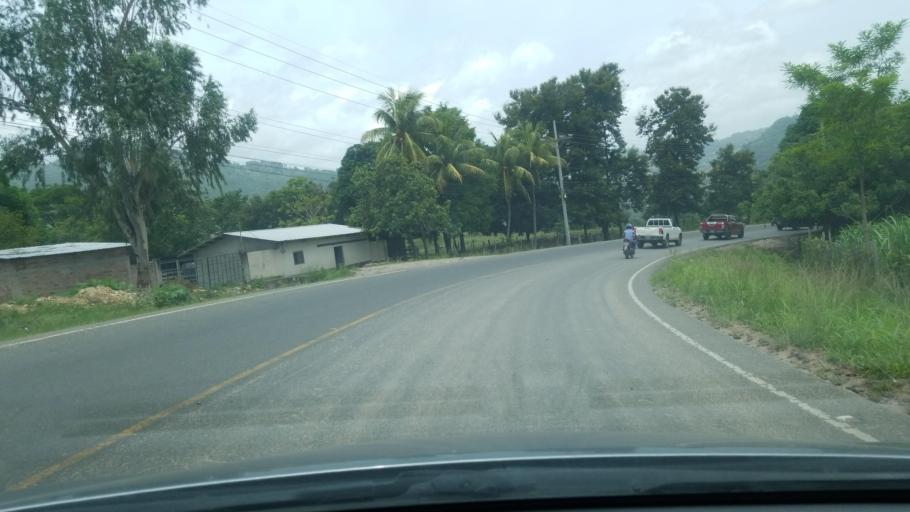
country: HN
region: Copan
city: Santa Rosa de Copan
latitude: 14.7244
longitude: -88.7671
